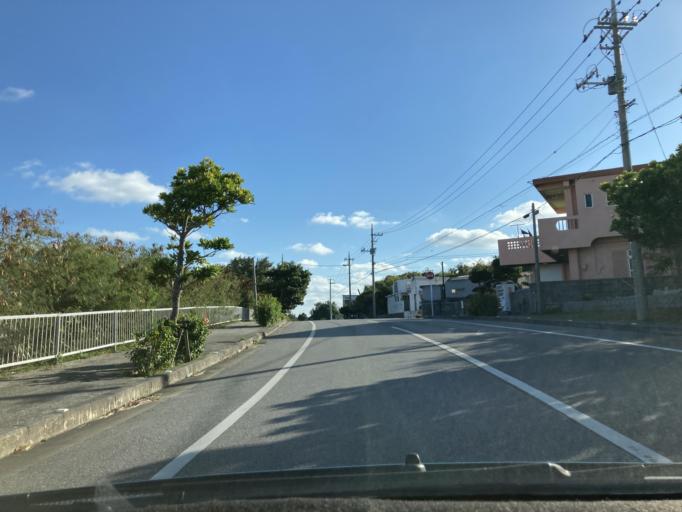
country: JP
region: Okinawa
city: Katsuren-haebaru
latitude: 26.3084
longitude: 127.9204
